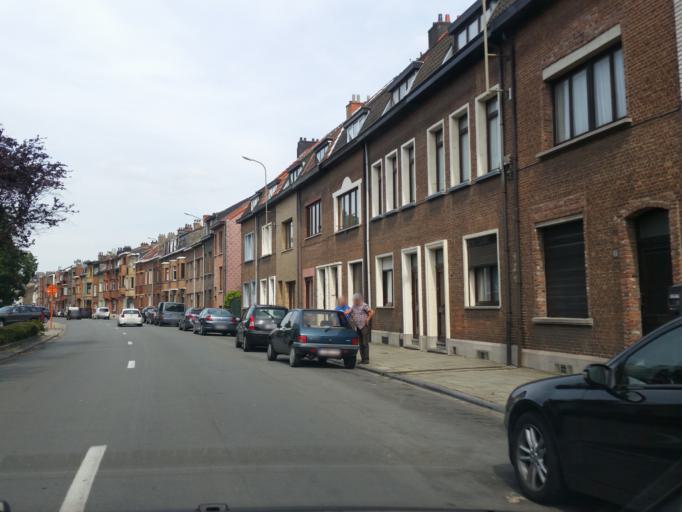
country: BE
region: Flanders
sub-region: Provincie Vlaams-Brabant
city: Vilvoorde
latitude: 50.9222
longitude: 4.4297
